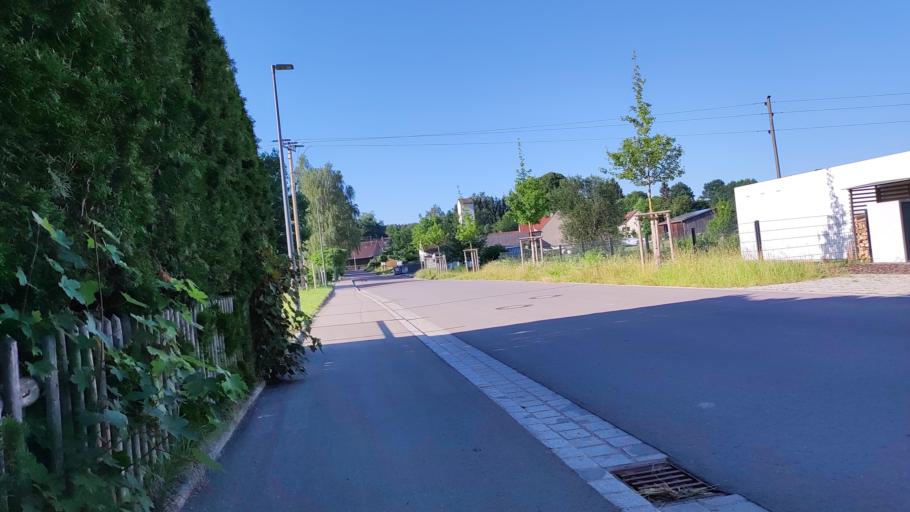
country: DE
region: Bavaria
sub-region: Swabia
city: Horgau
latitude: 48.3927
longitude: 10.6801
